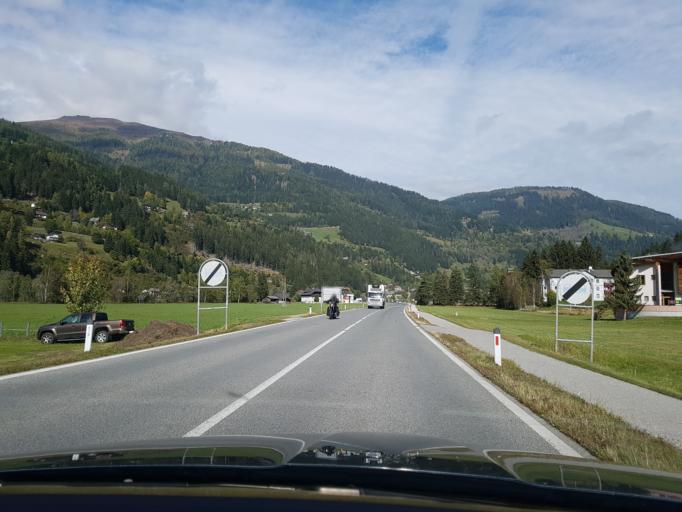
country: AT
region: Carinthia
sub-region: Politischer Bezirk Spittal an der Drau
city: Kleinkirchheim
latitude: 46.8197
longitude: 13.8626
